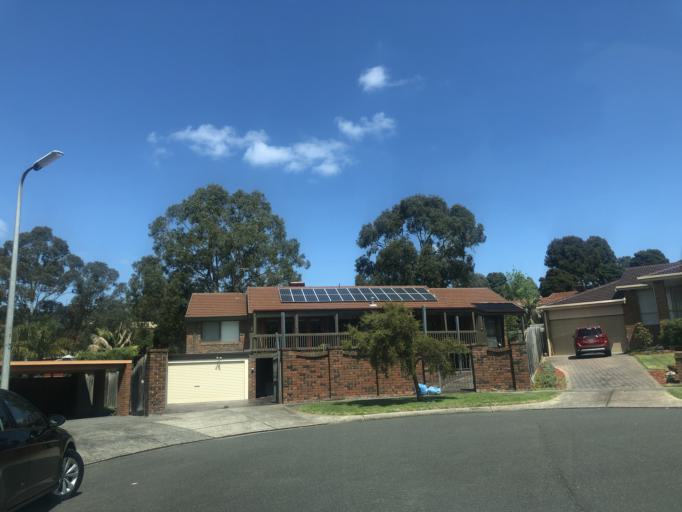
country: AU
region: Victoria
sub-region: Monash
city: Mulgrave
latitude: -37.9191
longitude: 145.1901
